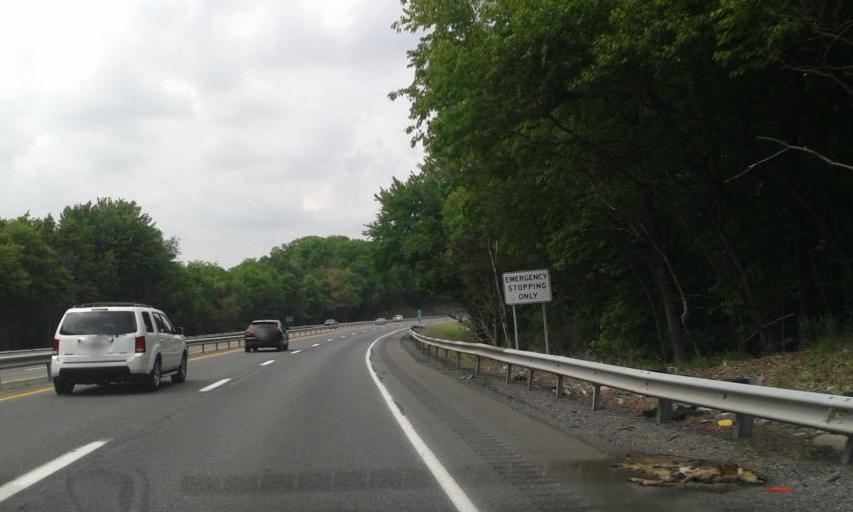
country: US
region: Pennsylvania
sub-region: Monroe County
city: Saylorsburg
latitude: 40.8736
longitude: -75.3134
